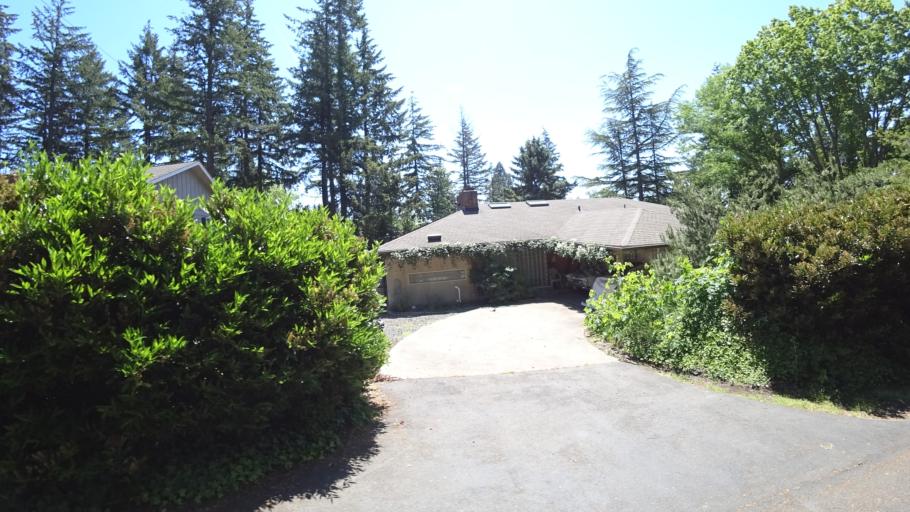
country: US
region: Oregon
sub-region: Washington County
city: Raleigh Hills
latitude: 45.4912
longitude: -122.7140
